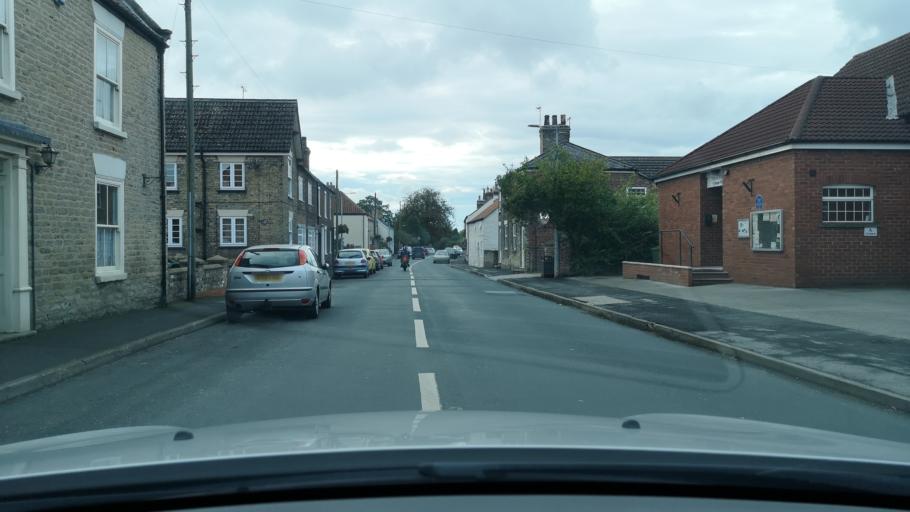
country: GB
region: England
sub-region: East Riding of Yorkshire
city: North Cave
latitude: 53.7794
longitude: -0.6502
